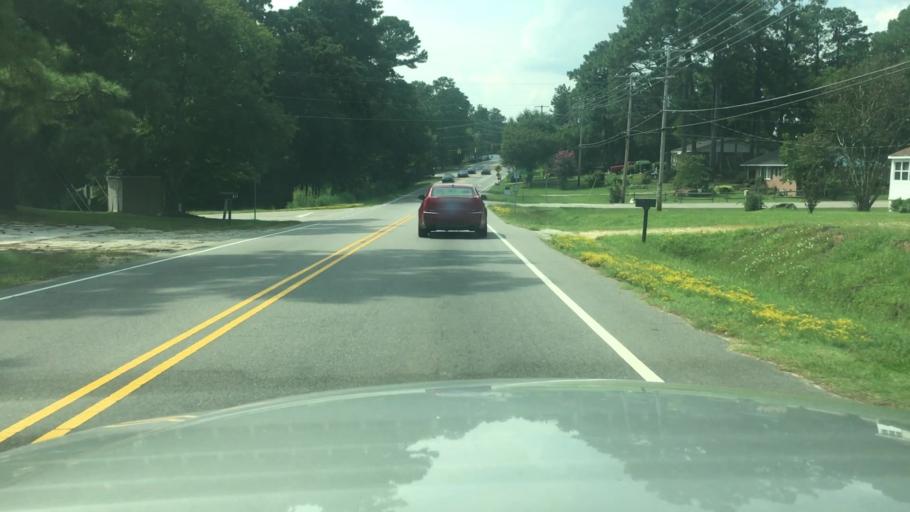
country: US
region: North Carolina
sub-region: Cumberland County
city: Fayetteville
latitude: 35.1171
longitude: -78.9111
